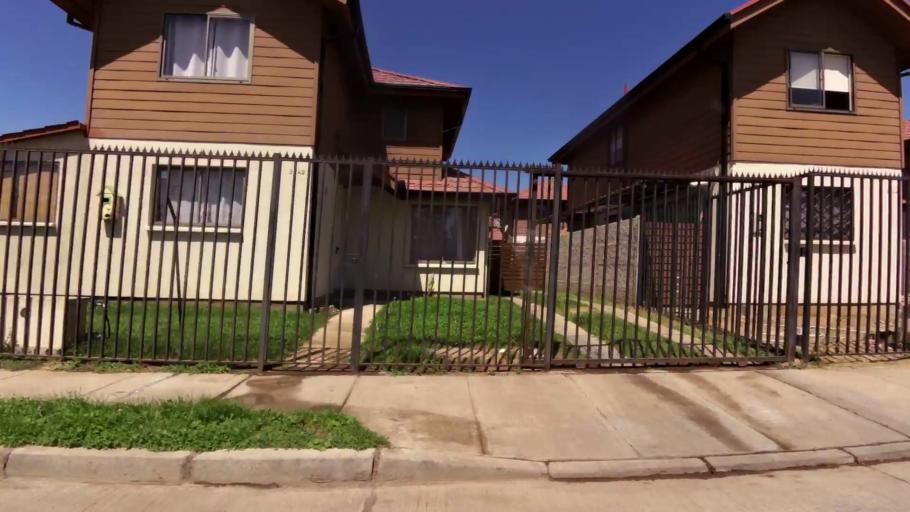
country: CL
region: Maule
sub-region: Provincia de Talca
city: Talca
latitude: -35.4303
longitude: -71.6057
